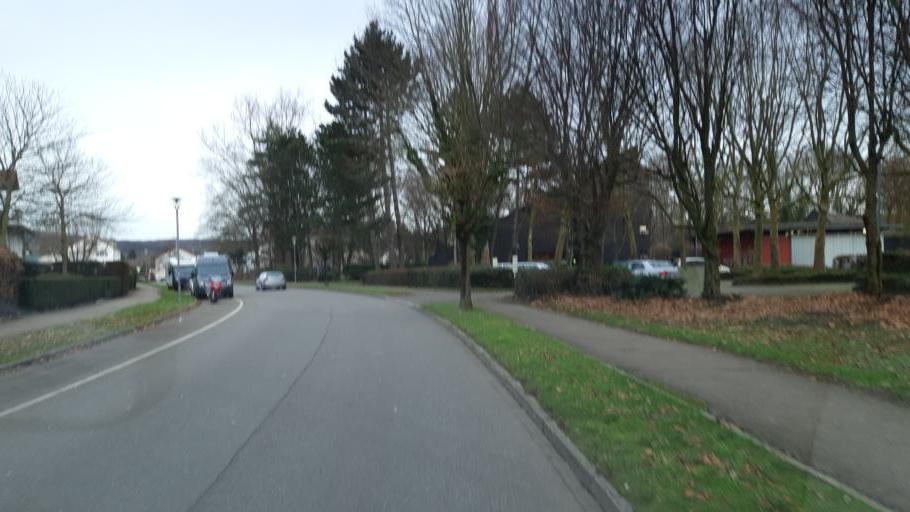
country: DE
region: Baden-Wuerttemberg
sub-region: Freiburg Region
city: Emmendingen
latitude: 48.1082
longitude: 7.8591
